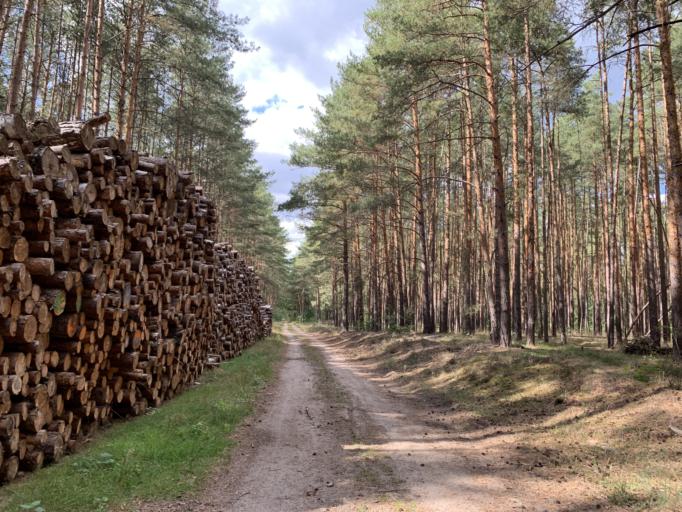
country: DE
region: Brandenburg
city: Michendorf
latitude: 52.3179
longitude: 13.0060
